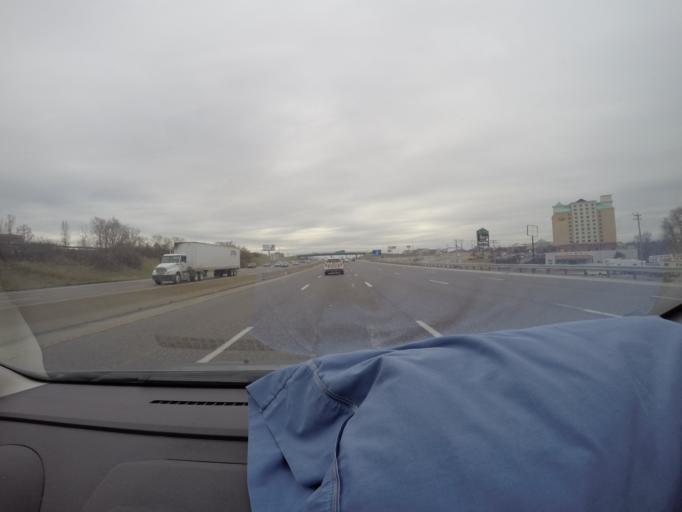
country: US
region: Missouri
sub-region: Saint Charles County
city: Saint Charles
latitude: 38.7722
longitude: -90.5037
